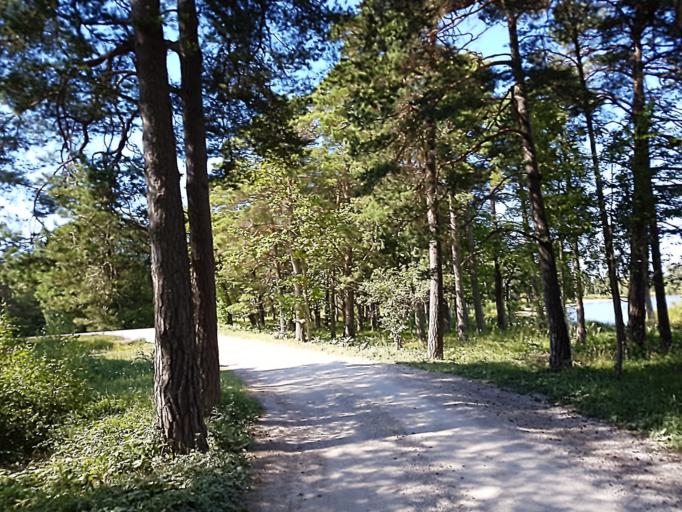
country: SE
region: Gotland
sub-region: Gotland
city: Visby
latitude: 57.6010
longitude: 18.3544
